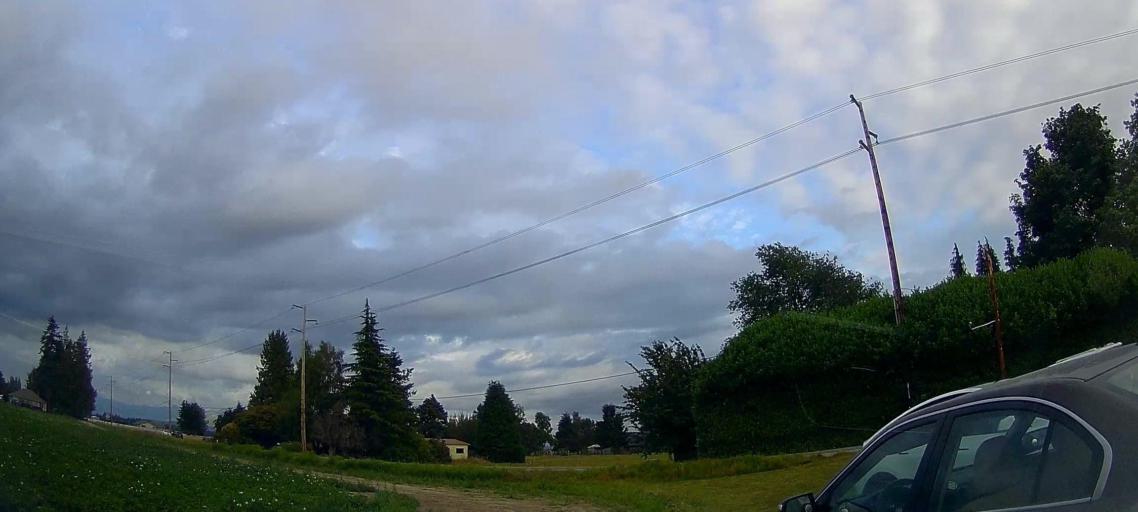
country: US
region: Washington
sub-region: Skagit County
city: Burlington
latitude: 48.5164
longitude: -122.4319
